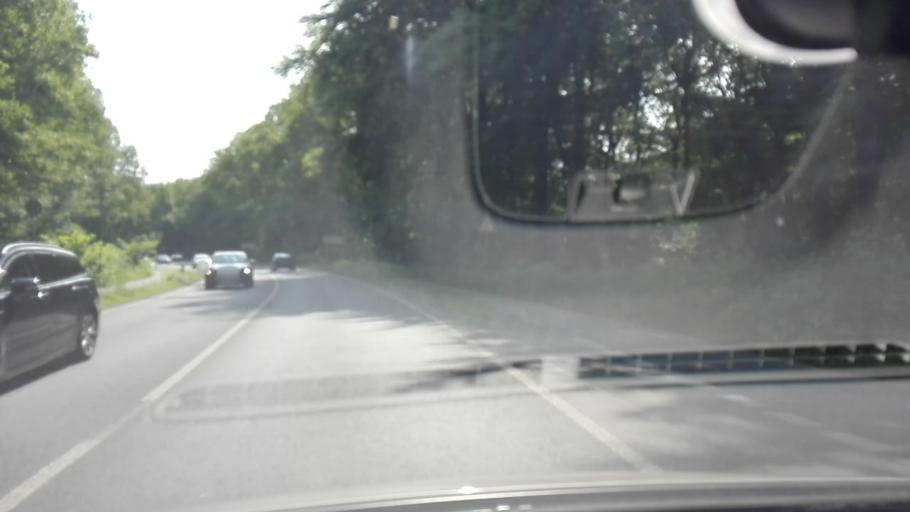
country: DE
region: North Rhine-Westphalia
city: Lunen
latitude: 51.6088
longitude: 7.5365
